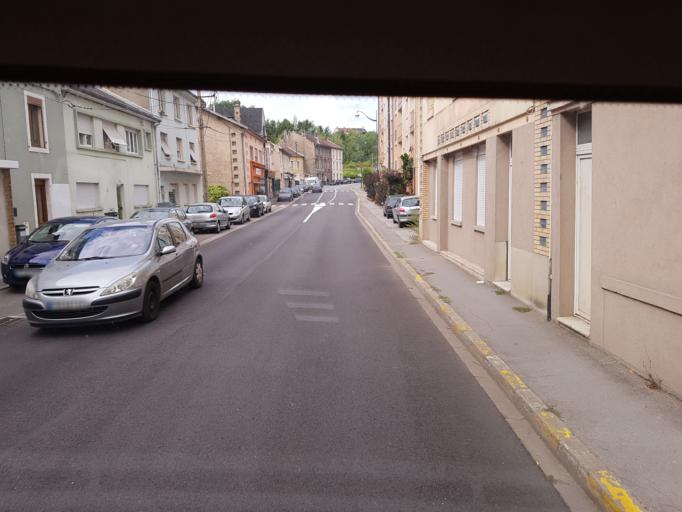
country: FR
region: Lorraine
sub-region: Departement de Meurthe-et-Moselle
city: Joeuf
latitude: 49.2236
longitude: 6.0121
